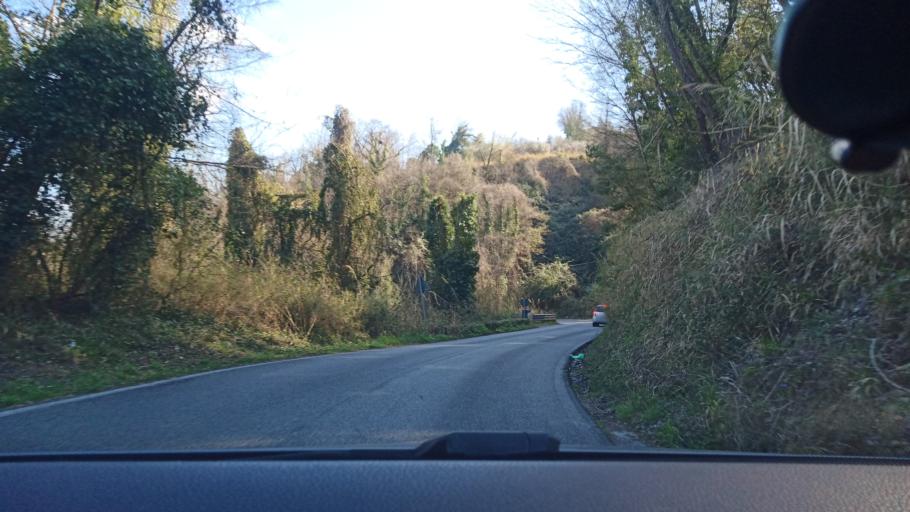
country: IT
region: Latium
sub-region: Citta metropolitana di Roma Capitale
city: Torrita Tiberina
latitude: 42.2428
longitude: 12.6207
